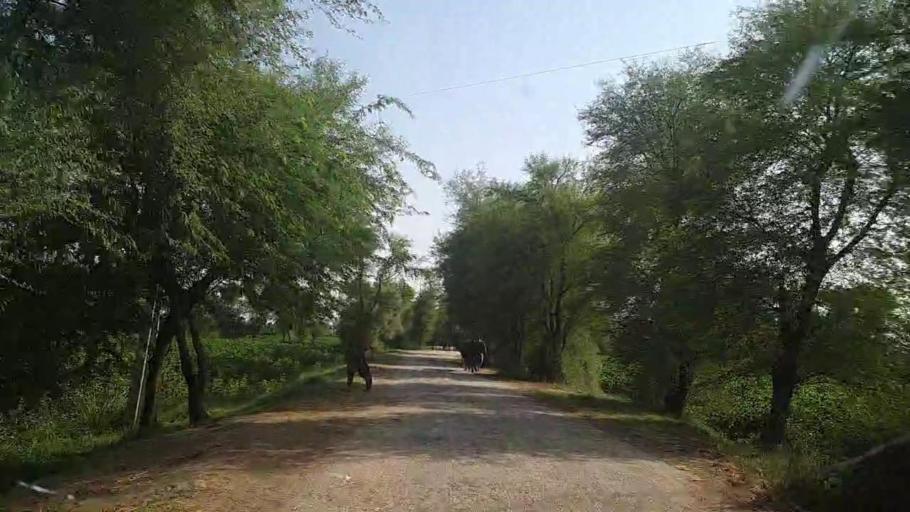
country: PK
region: Sindh
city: Khanpur
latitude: 27.7312
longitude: 69.3325
